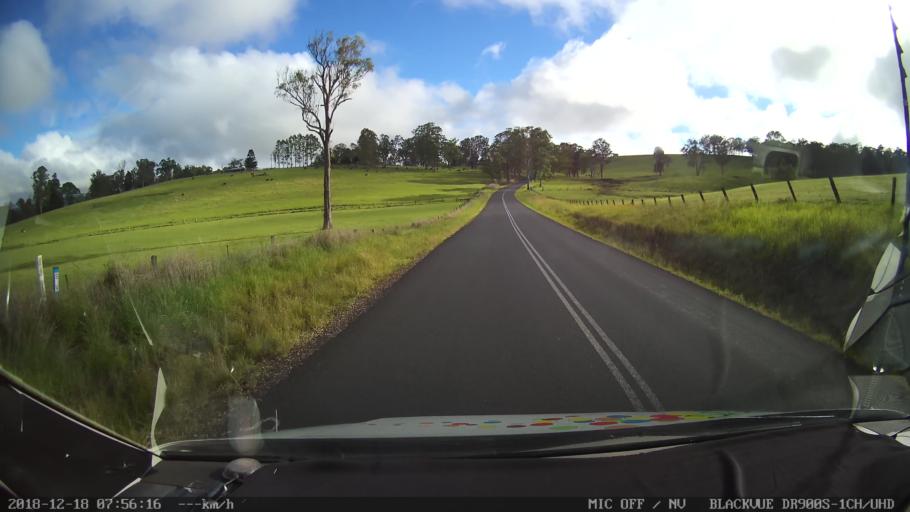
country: AU
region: New South Wales
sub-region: Kyogle
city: Kyogle
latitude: -28.4004
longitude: 152.6049
